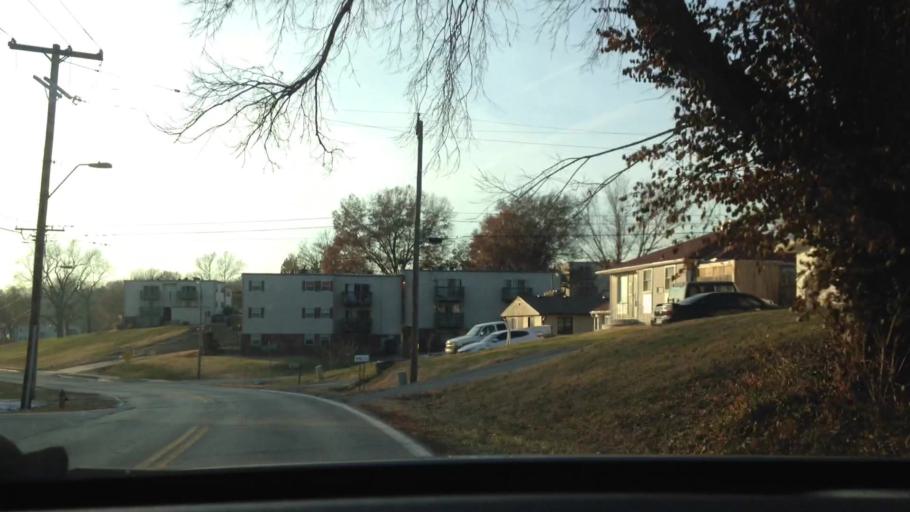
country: US
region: Missouri
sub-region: Clay County
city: North Kansas City
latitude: 39.1609
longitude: -94.5416
